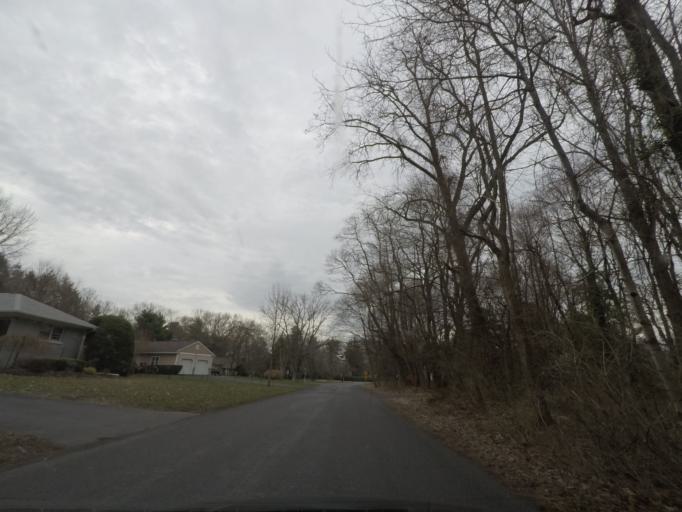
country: US
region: New York
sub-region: Albany County
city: Delmar
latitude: 42.6110
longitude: -73.8415
